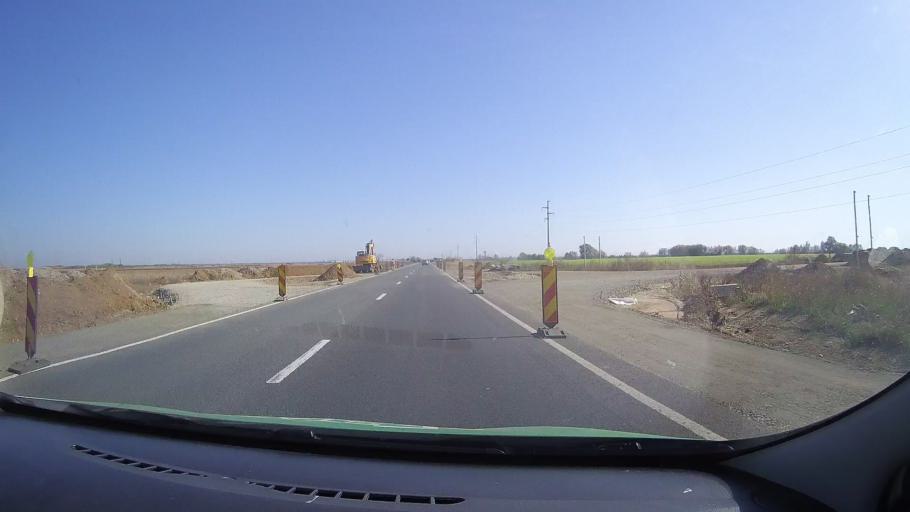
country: RO
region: Satu Mare
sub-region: Comuna Capleni
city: Capleni
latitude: 47.6852
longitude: 22.5083
